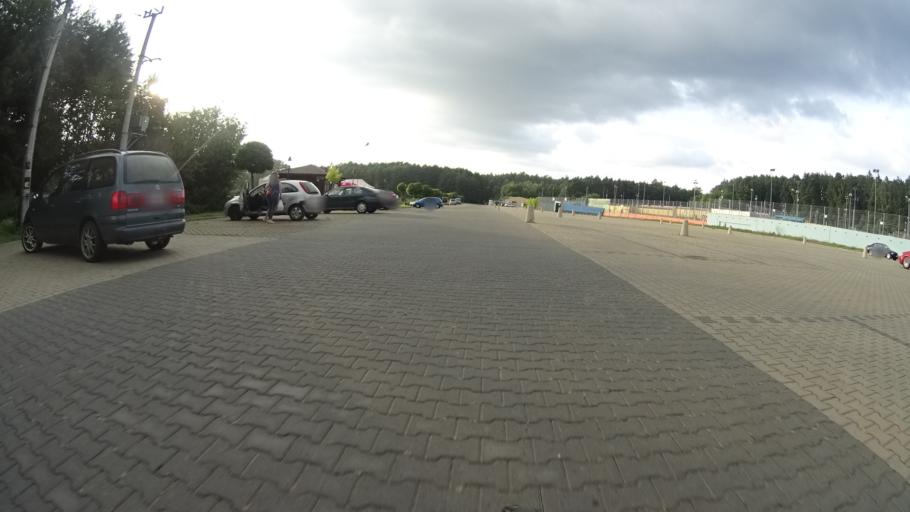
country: PL
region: Masovian Voivodeship
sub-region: Powiat grojecki
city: Mogielnica
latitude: 51.6969
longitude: 20.7261
